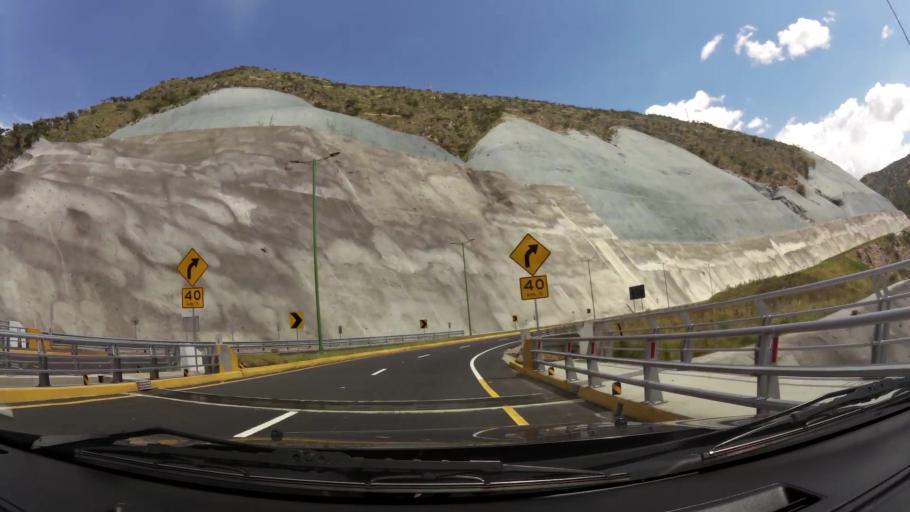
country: EC
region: Pichincha
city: Quito
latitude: -0.1058
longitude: -78.3831
